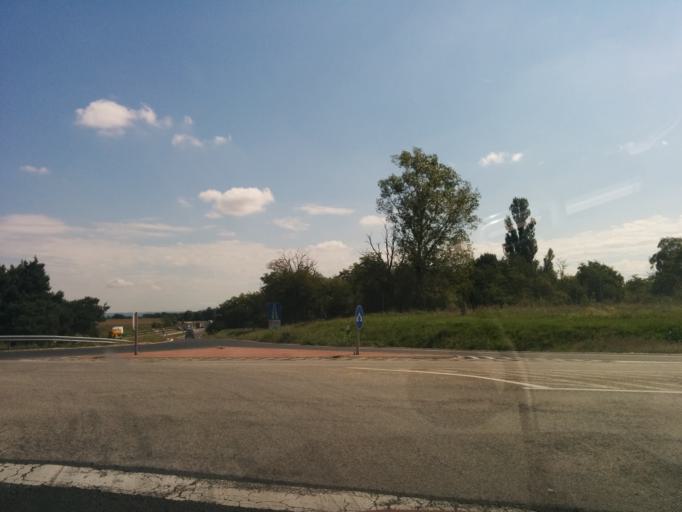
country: HU
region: Komarom-Esztergom
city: Nagyigmand
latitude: 47.6742
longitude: 18.0911
